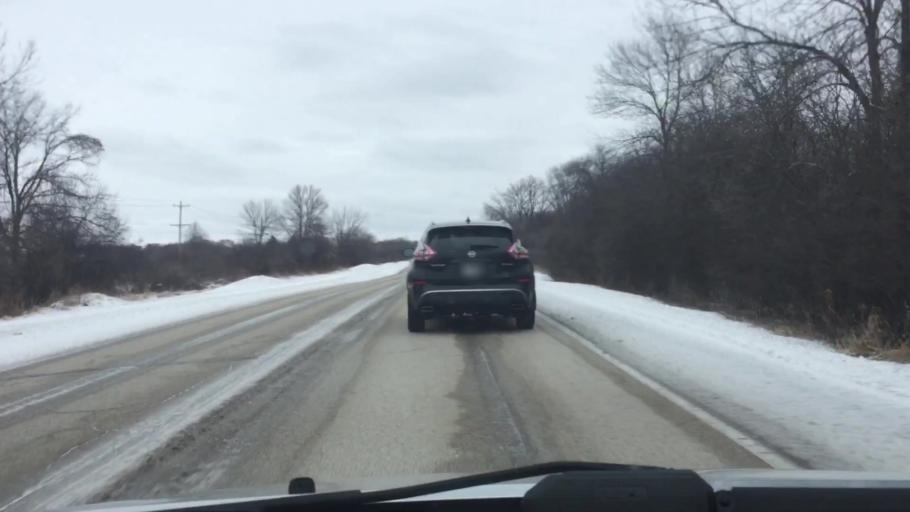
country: US
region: Wisconsin
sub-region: Waukesha County
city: Brookfield
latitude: 43.0462
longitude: -88.1061
